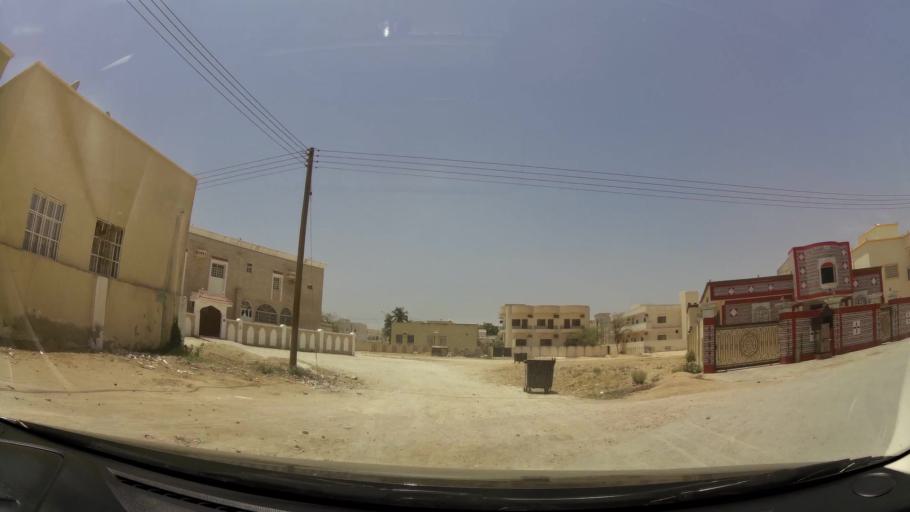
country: OM
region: Zufar
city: Salalah
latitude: 17.0711
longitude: 54.1563
